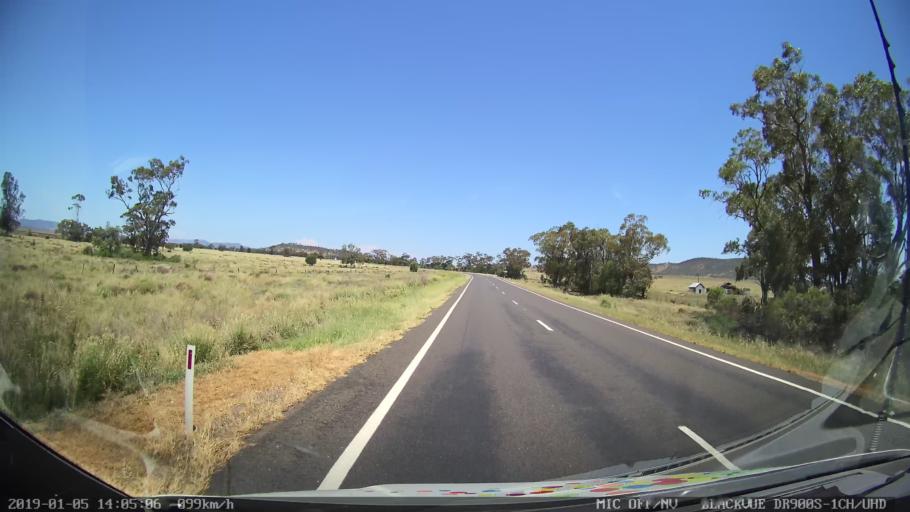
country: AU
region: New South Wales
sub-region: Gunnedah
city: Gunnedah
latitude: -31.2070
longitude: 150.3714
